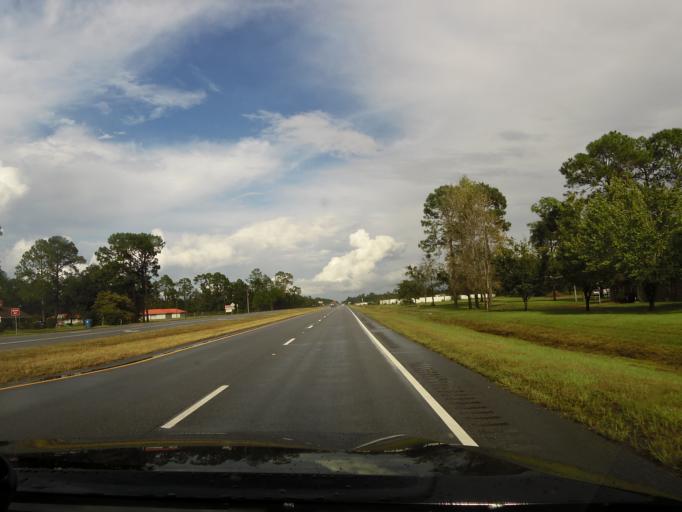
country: US
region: Georgia
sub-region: Liberty County
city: Walthourville
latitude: 31.7636
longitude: -81.6514
